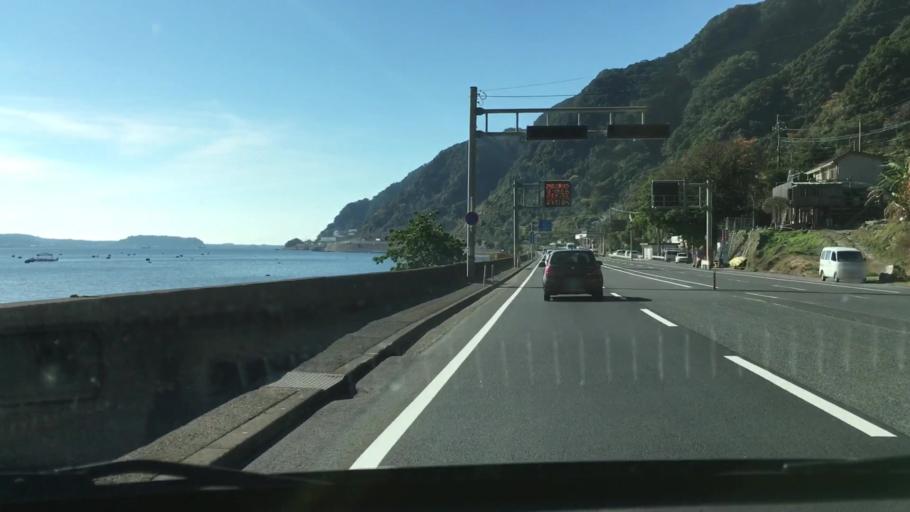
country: JP
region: Kagoshima
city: Kagoshima-shi
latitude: 31.6497
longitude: 130.6059
